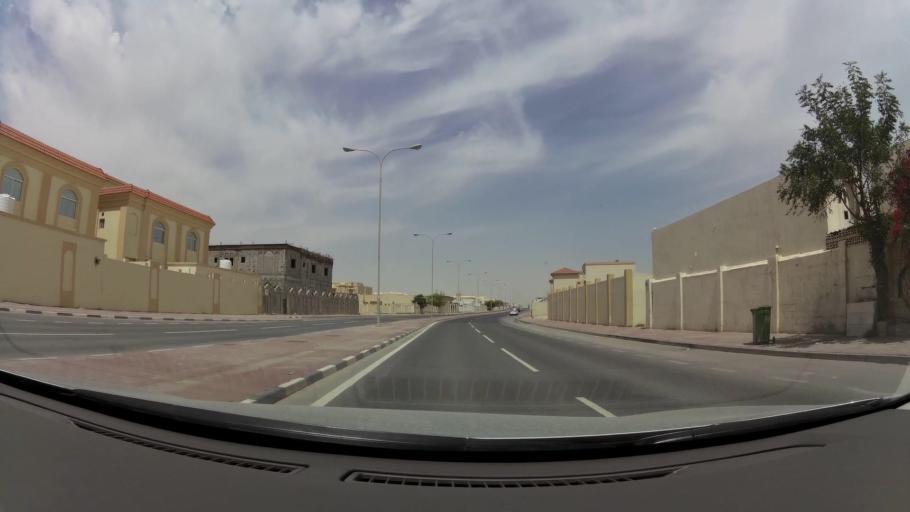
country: QA
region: Baladiyat ar Rayyan
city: Ar Rayyan
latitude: 25.2949
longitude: 51.4122
